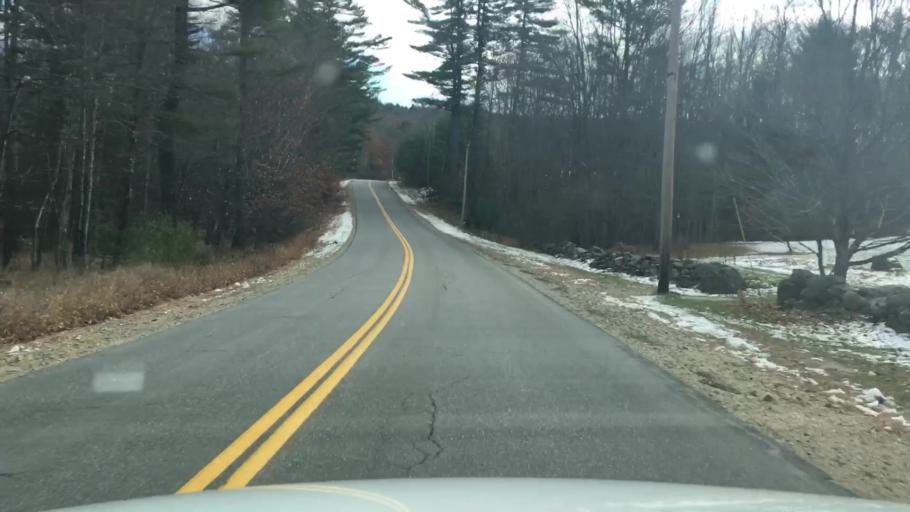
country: US
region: Maine
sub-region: Oxford County
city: Canton
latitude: 44.4903
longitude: -70.3263
